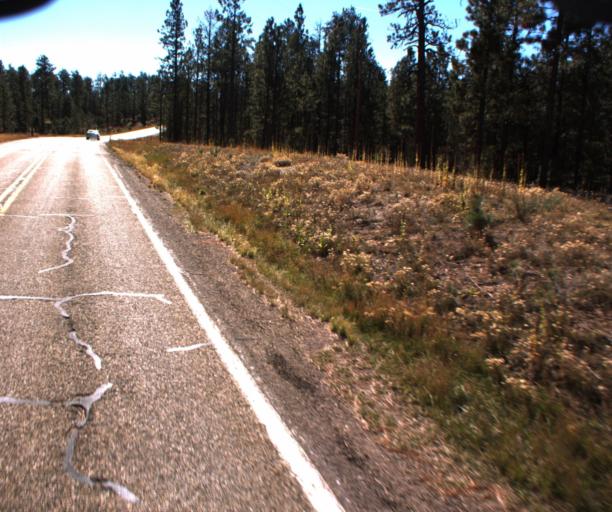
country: US
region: Arizona
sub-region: Coconino County
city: Fredonia
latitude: 36.7347
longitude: -112.2137
